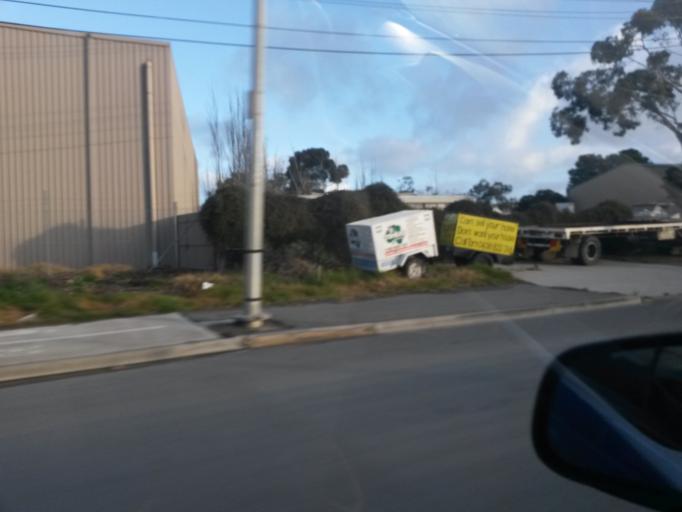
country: AU
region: South Australia
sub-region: Port Adelaide Enfield
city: Alberton
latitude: -34.8402
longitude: 138.5176
